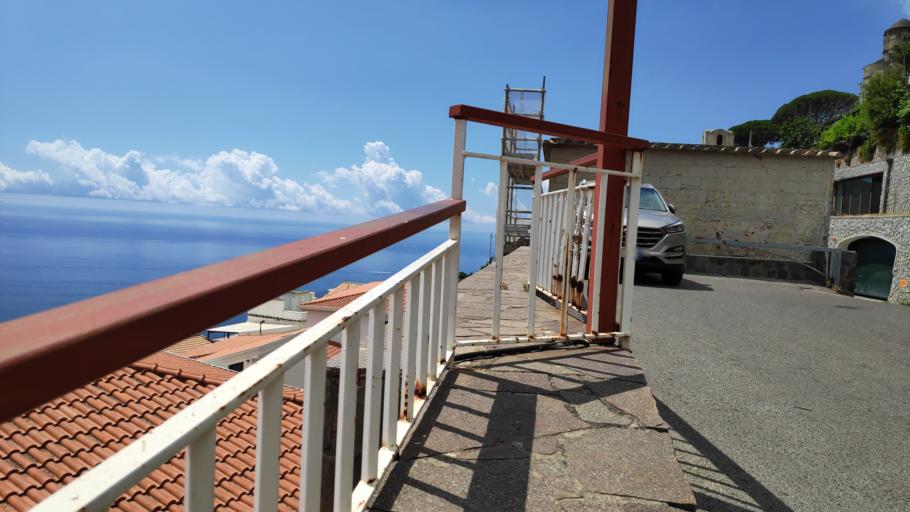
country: IT
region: Campania
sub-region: Provincia di Salerno
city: Ravello
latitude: 40.6490
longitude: 14.6144
